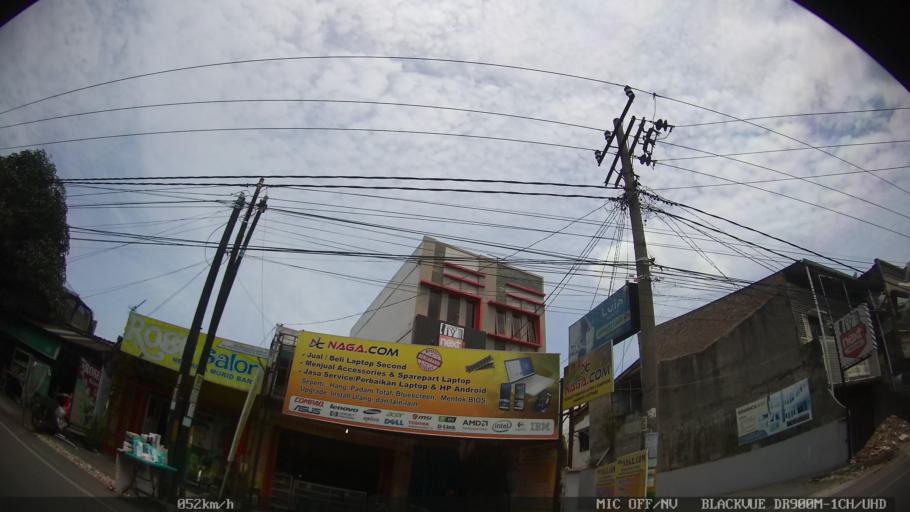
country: ID
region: North Sumatra
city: Medan
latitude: 3.5539
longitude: 98.6607
